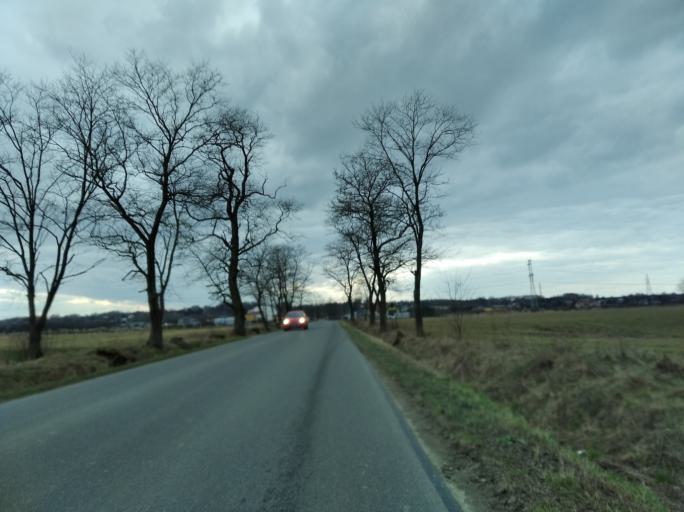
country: PL
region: Subcarpathian Voivodeship
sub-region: Powiat krosnienski
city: Odrzykon
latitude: 49.7533
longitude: 21.7122
